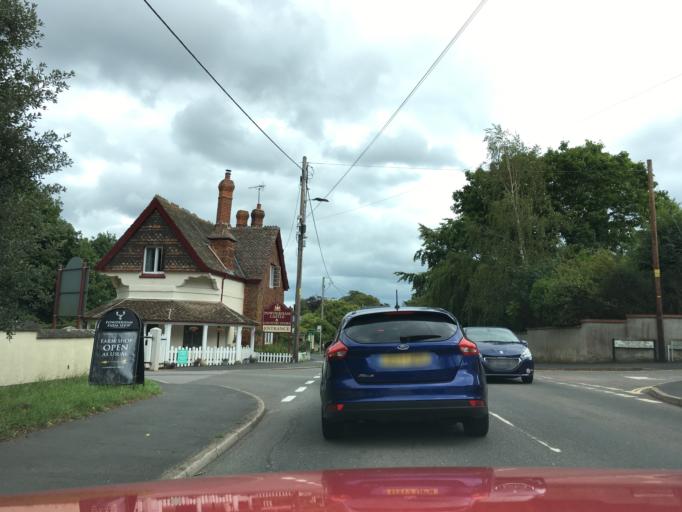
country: GB
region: England
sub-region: Devon
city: Starcross
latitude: 50.6388
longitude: -3.4663
